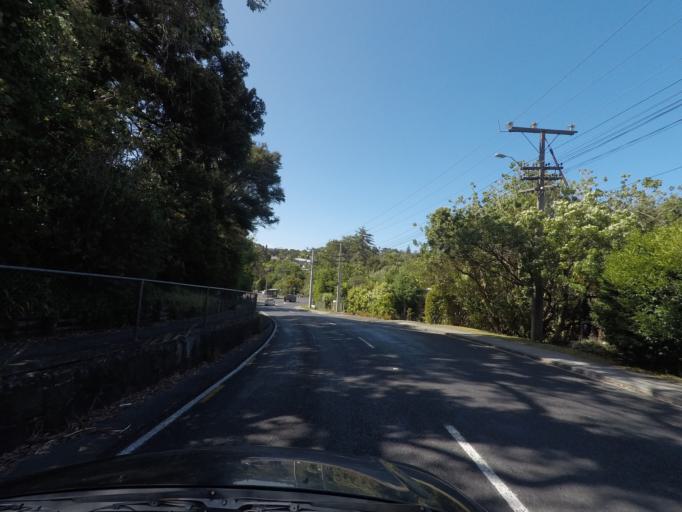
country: NZ
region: Auckland
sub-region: Auckland
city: Waitakere
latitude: -36.9251
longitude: 174.6554
